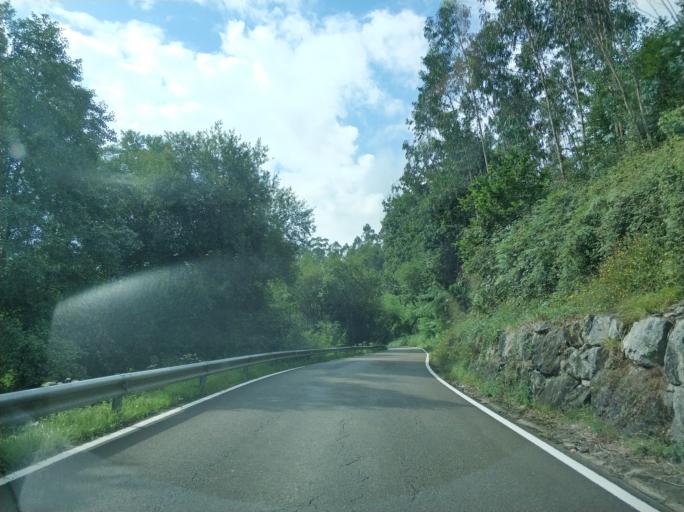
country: ES
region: Cantabria
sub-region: Provincia de Cantabria
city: Polanco
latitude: 43.3762
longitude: -3.9713
